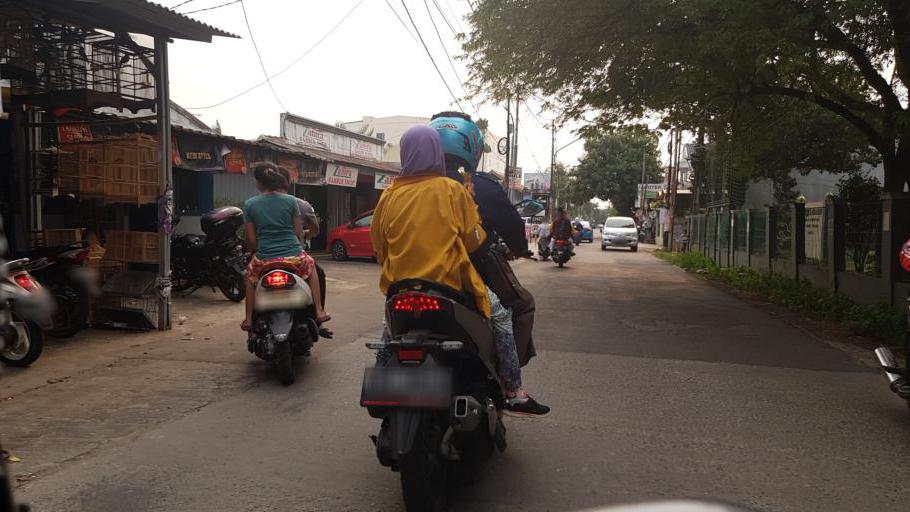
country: ID
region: West Java
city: Depok
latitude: -6.3725
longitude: 106.8453
